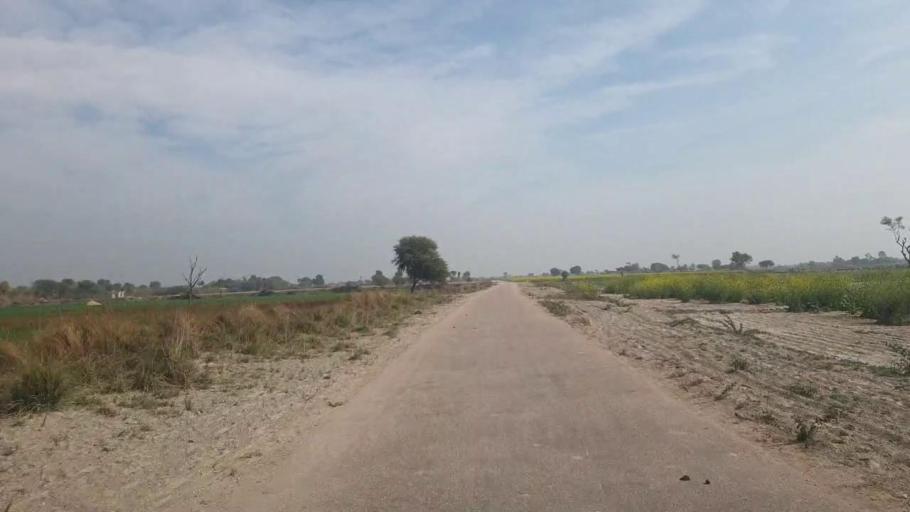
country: PK
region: Sindh
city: Nawabshah
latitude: 26.1240
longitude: 68.4941
